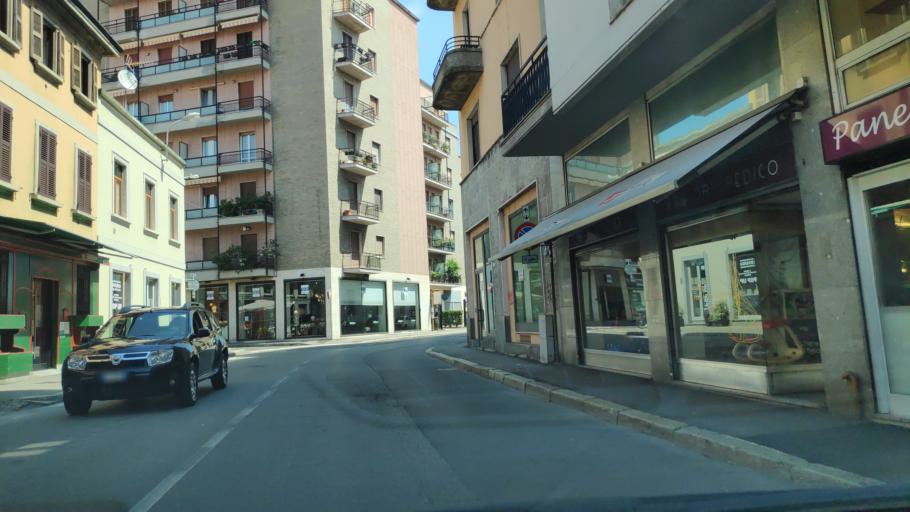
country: IT
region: Lombardy
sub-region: Provincia di Monza e Brianza
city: Monza
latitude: 45.5868
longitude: 9.2704
